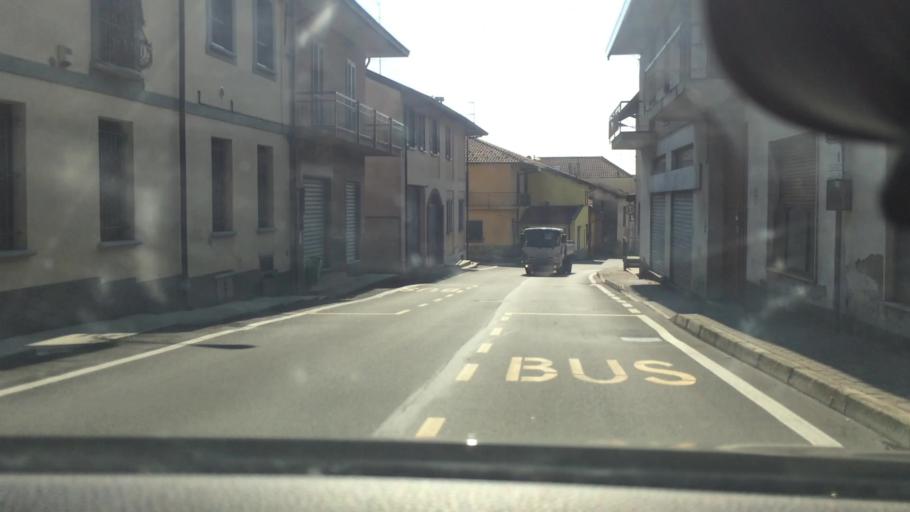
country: IT
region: Lombardy
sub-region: Citta metropolitana di Milano
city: Bernate Ticino
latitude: 45.4792
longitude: 8.8196
